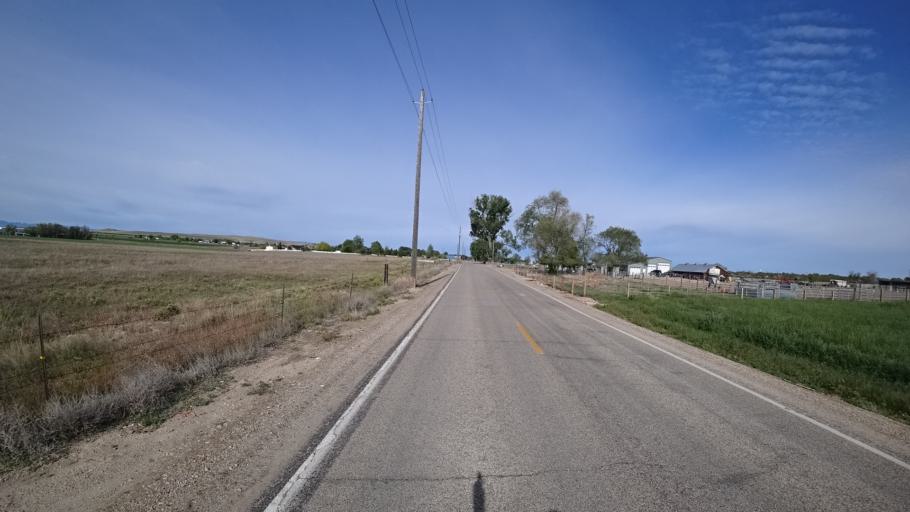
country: US
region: Idaho
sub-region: Ada County
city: Kuna
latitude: 43.4738
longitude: -116.3901
